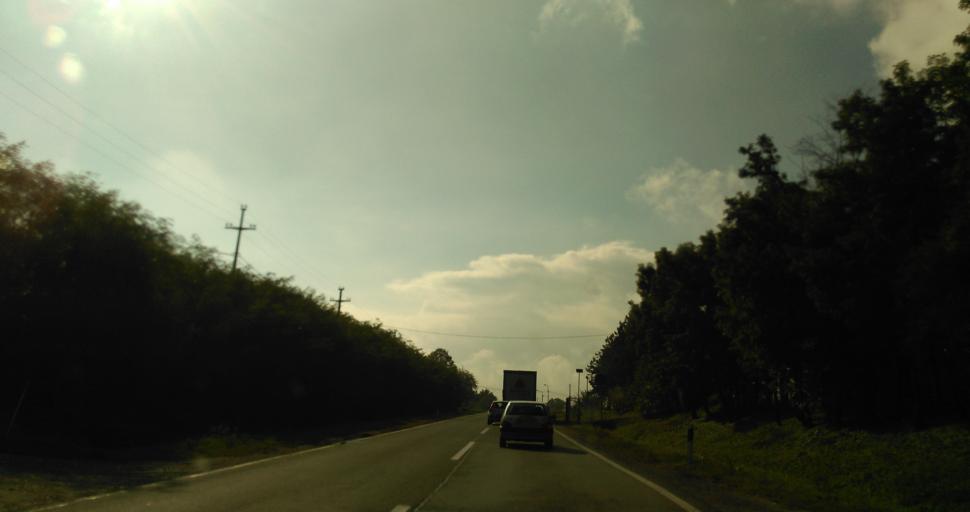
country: RS
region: Central Serbia
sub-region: Kolubarski Okrug
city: Lajkovac
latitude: 44.3554
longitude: 20.1903
